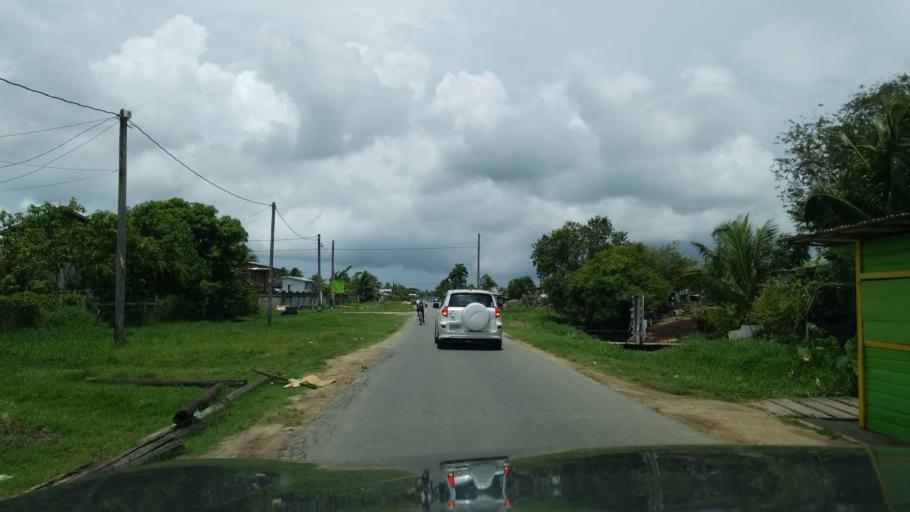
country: GY
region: Demerara-Mahaica
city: Georgetown
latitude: 6.7996
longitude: -58.1239
